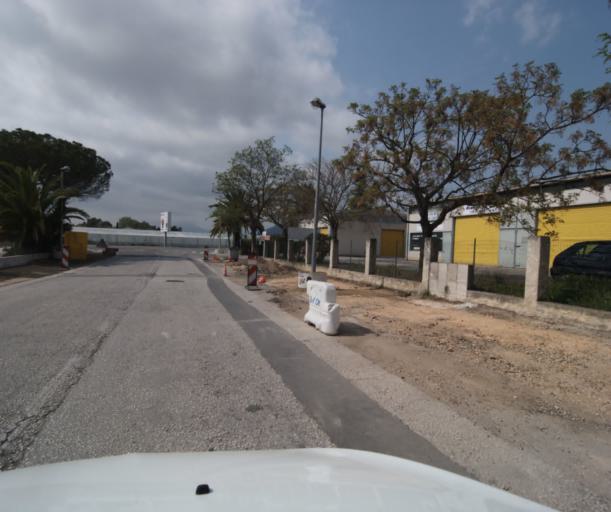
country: FR
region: Provence-Alpes-Cote d'Azur
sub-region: Departement du Var
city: Hyeres
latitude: 43.1038
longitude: 6.1414
